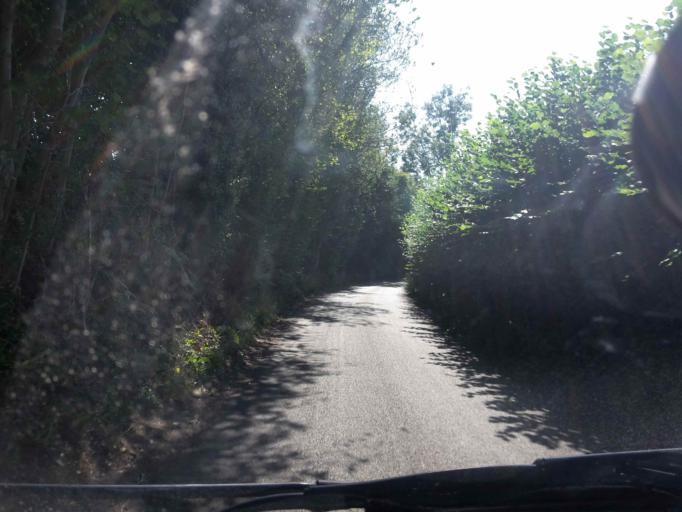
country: GB
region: England
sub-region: Surrey
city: Cranleigh
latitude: 51.1926
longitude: -0.4818
